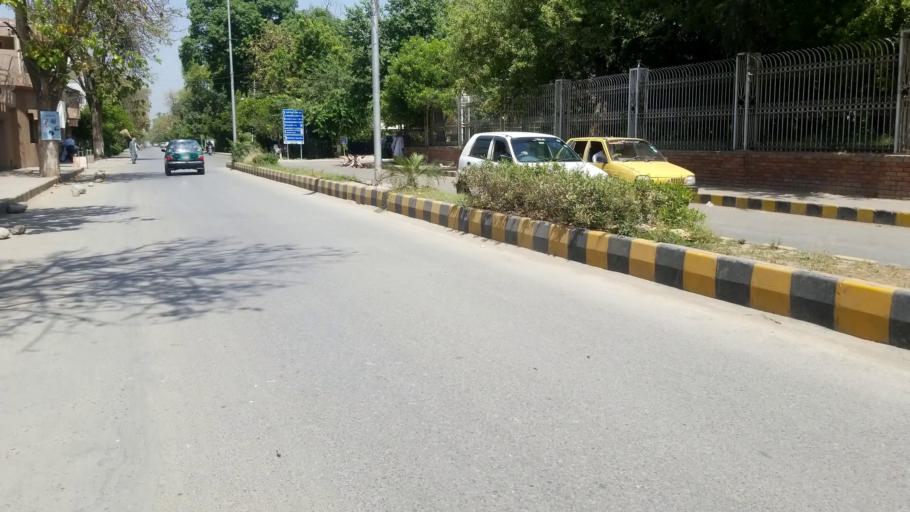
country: PK
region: Khyber Pakhtunkhwa
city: Peshawar
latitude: 33.9993
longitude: 71.4862
